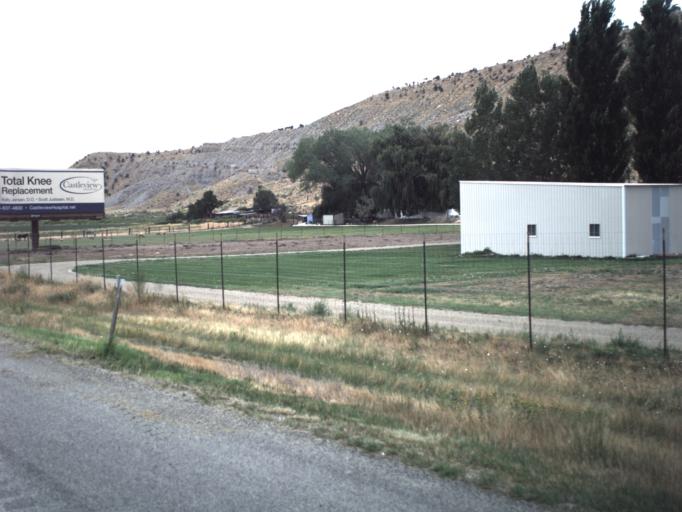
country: US
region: Utah
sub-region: Carbon County
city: Spring Glen
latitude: 39.6709
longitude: -110.8616
